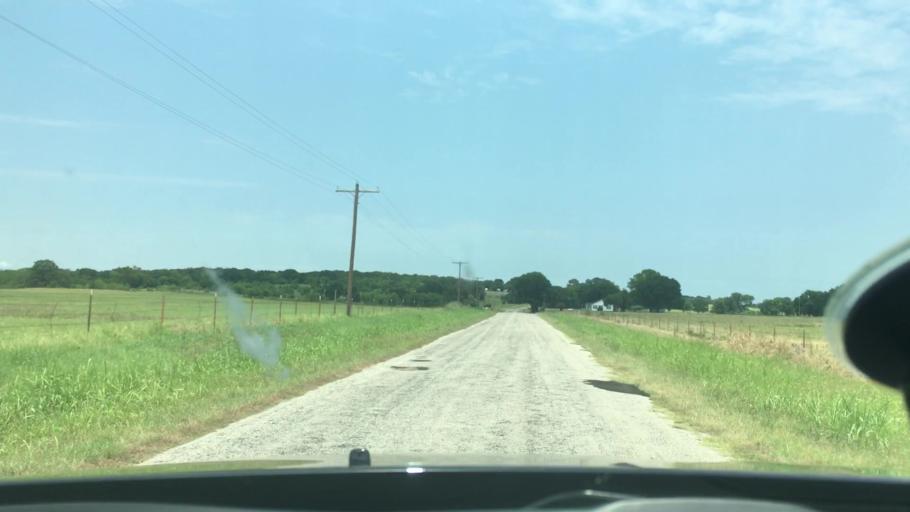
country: US
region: Texas
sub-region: Cooke County
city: Muenster
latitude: 33.8777
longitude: -97.3565
